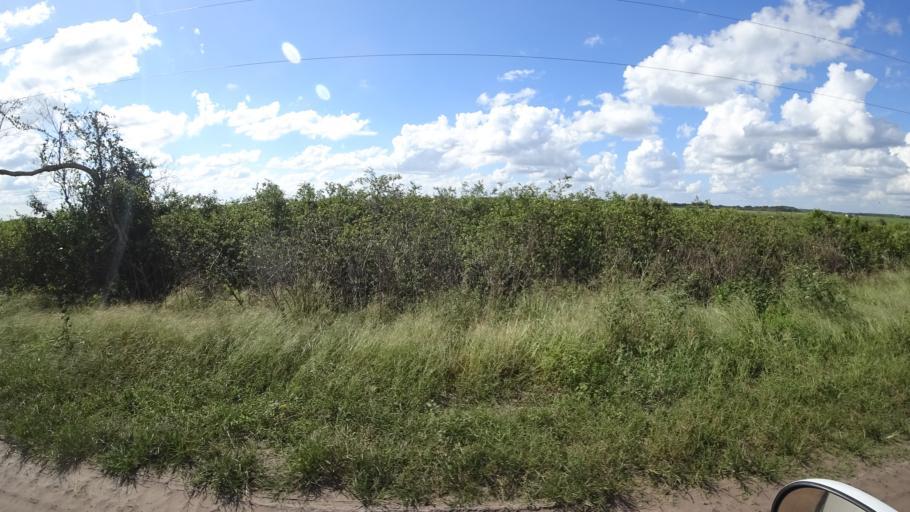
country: US
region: Florida
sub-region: DeSoto County
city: Arcadia
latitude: 27.3321
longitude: -82.0969
